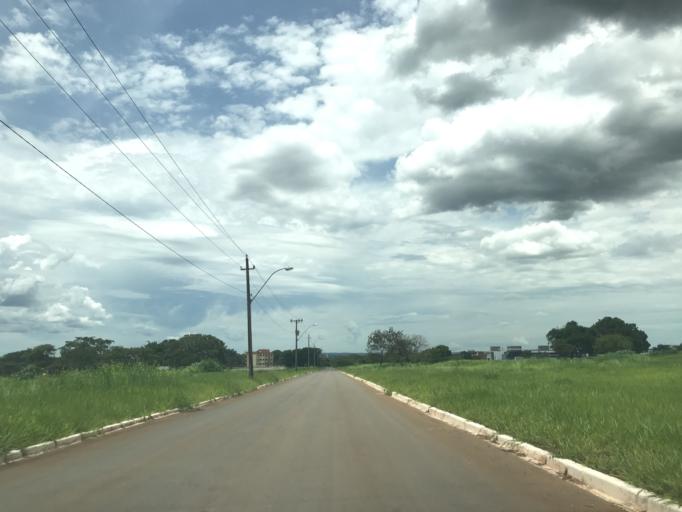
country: BR
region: Federal District
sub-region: Brasilia
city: Brasilia
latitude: -15.8326
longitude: -47.9046
